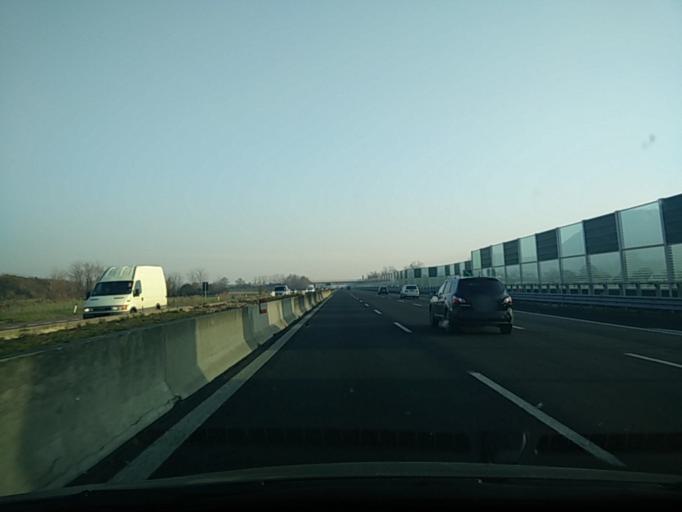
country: IT
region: Lombardy
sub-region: Provincia di Brescia
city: Capriolo
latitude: 45.6093
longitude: 9.9386
